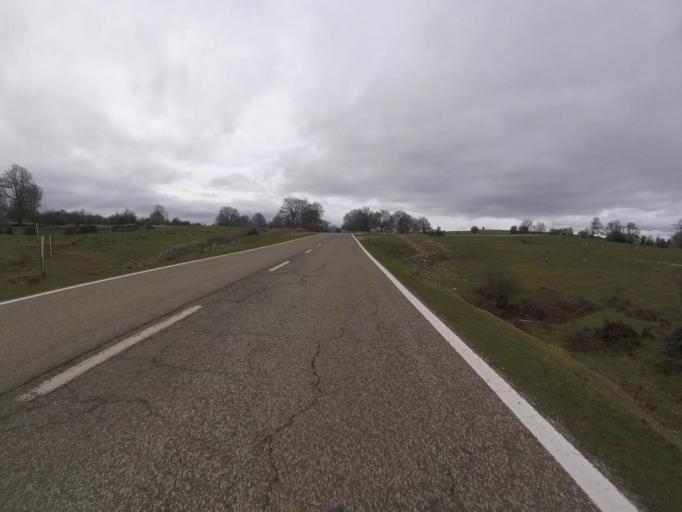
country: ES
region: Navarre
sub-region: Provincia de Navarra
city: Eulate
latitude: 42.7998
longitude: -2.1449
